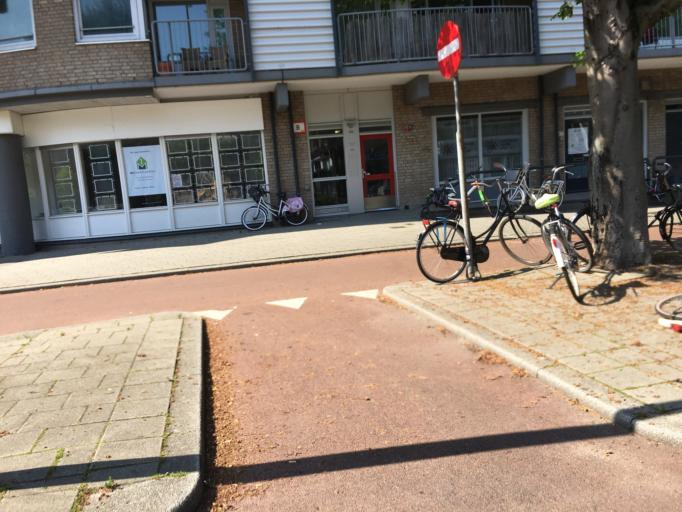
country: NL
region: South Holland
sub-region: Gemeente Rotterdam
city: Rotterdam
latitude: 51.9269
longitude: 4.4852
